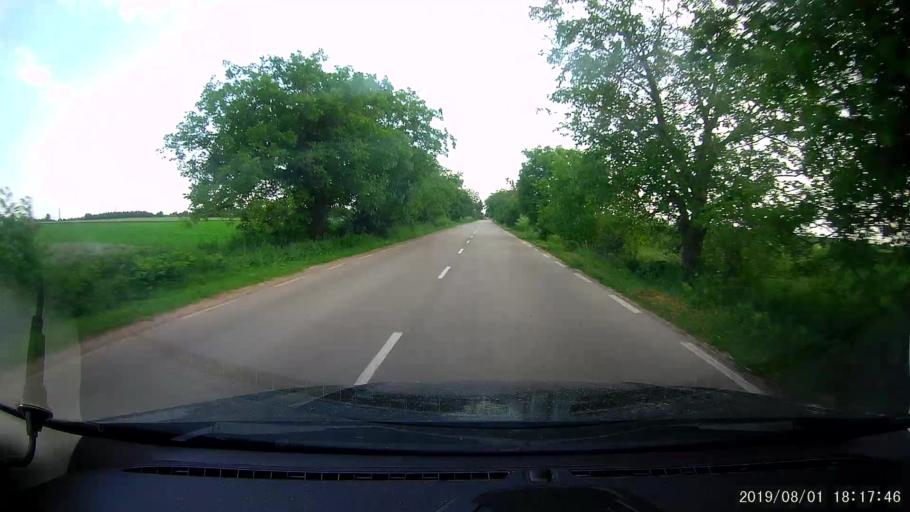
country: BG
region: Shumen
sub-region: Obshtina Kaolinovo
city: Kaolinovo
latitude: 43.7070
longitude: 27.0816
